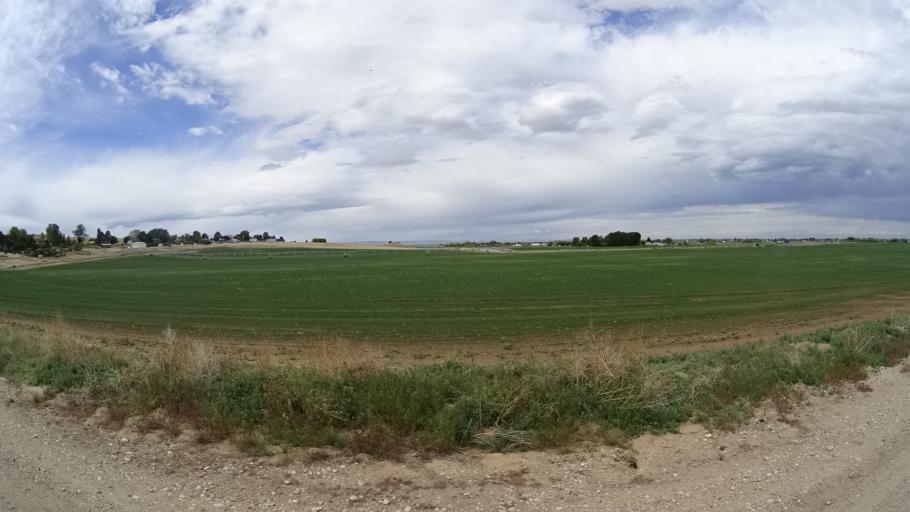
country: US
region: Idaho
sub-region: Ada County
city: Kuna
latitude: 43.4626
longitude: -116.4436
